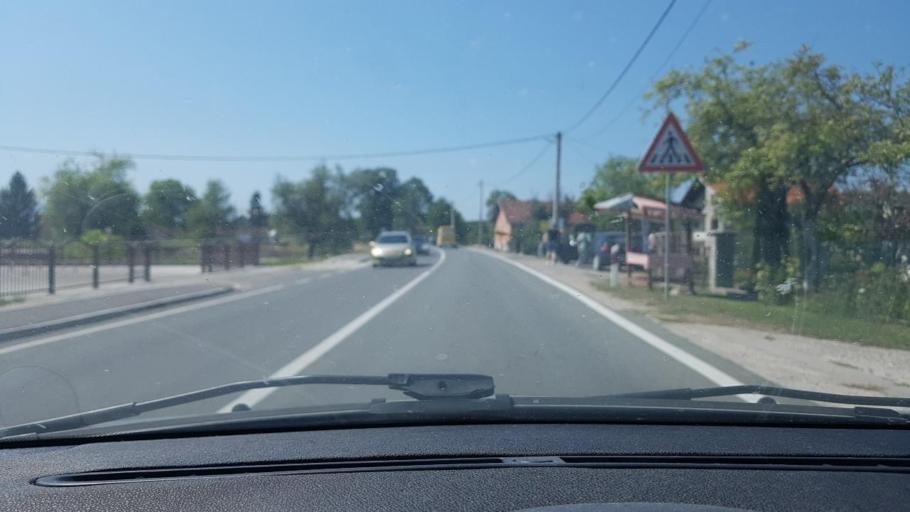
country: BA
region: Federation of Bosnia and Herzegovina
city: Bihac
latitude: 44.7914
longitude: 15.9279
